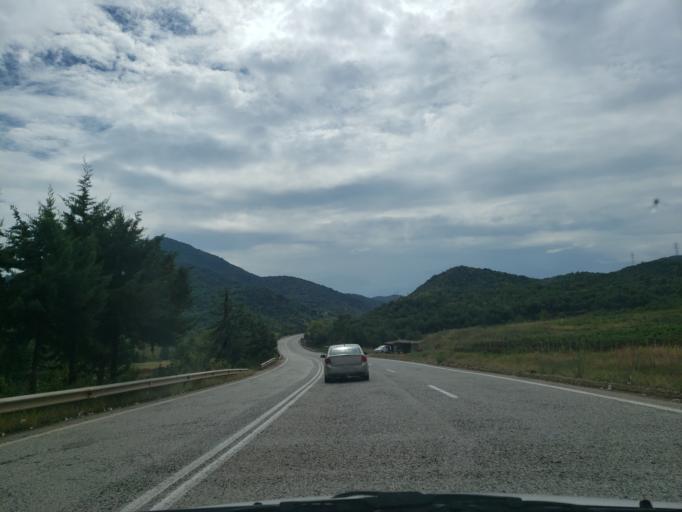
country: GR
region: Central Greece
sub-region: Nomos Fthiotidos
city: Stavros
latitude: 39.0165
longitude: 22.3764
